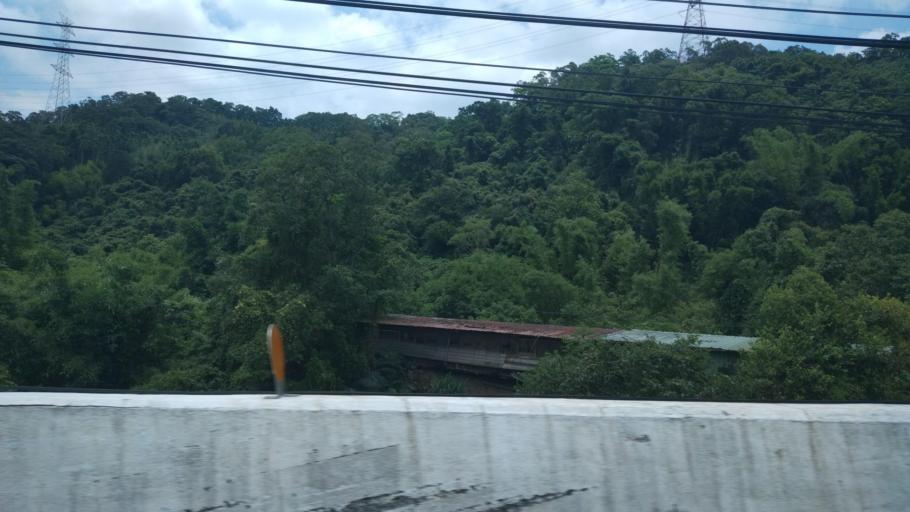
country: TW
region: Taipei
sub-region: Taipei
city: Banqiao
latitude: 24.9269
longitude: 121.4450
